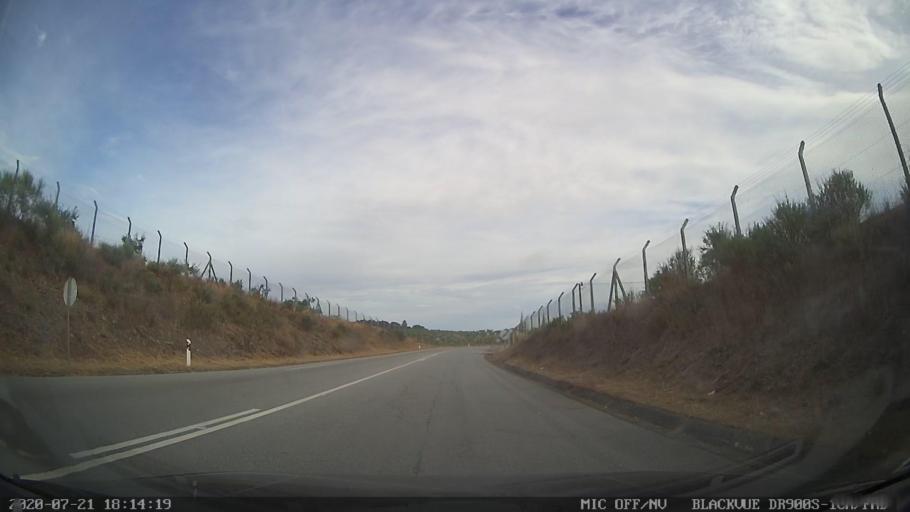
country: PT
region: Viseu
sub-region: Sao Joao da Pesqueira
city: Sao Joao da Pesqueira
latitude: 41.1249
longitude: -7.3912
